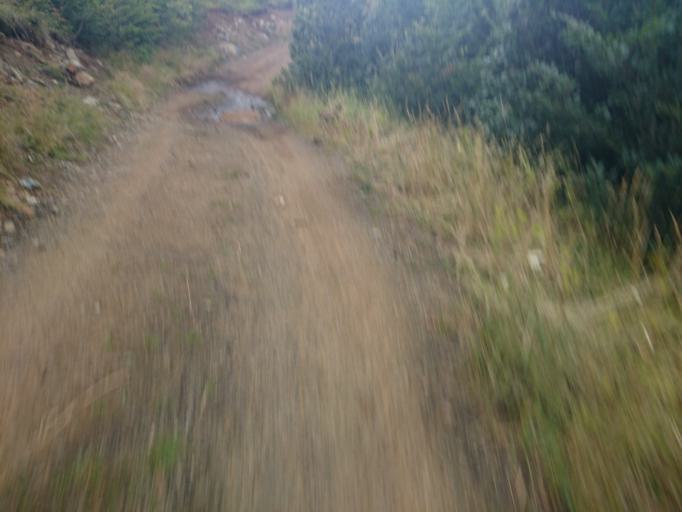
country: AL
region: Lezhe
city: Kurbnesh
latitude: 41.7860
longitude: 20.1486
